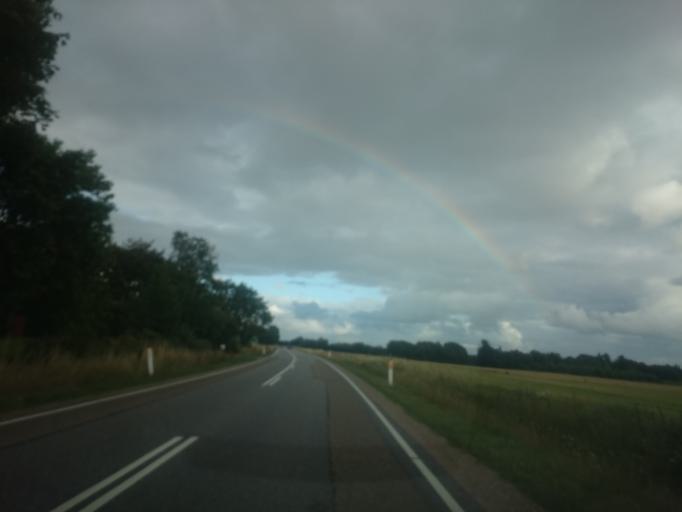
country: DK
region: South Denmark
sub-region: Billund Kommune
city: Grindsted
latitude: 55.6594
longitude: 8.7819
